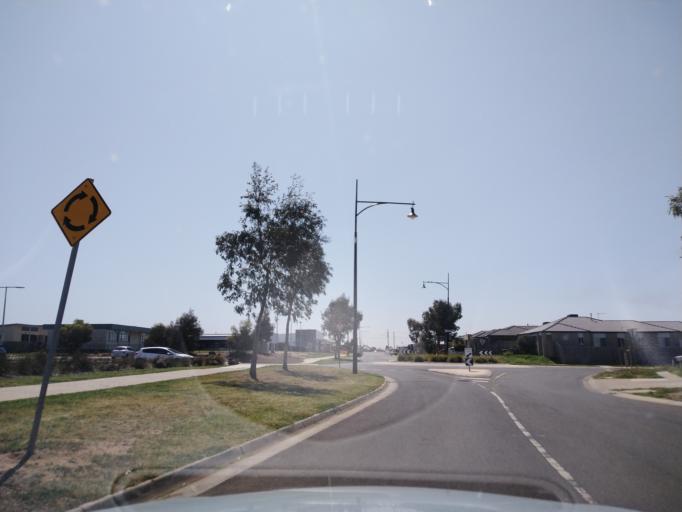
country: AU
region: Victoria
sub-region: Wyndham
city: Williams Landing
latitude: -37.8402
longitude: 144.7191
